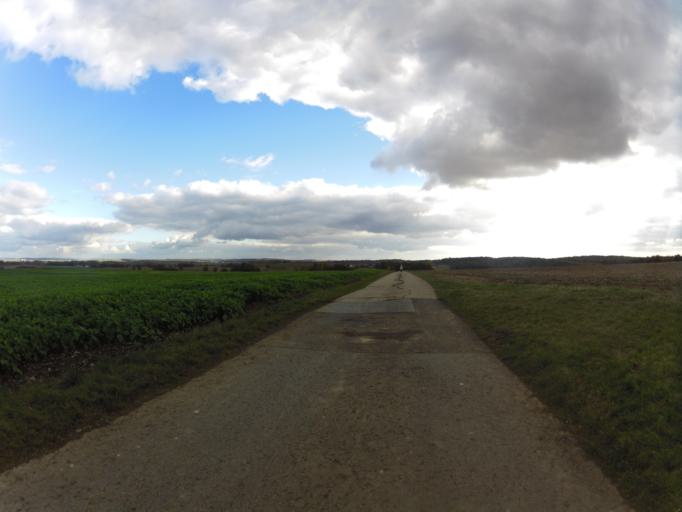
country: DE
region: Bavaria
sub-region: Regierungsbezirk Unterfranken
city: Kurnach
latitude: 49.8691
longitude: 10.0020
